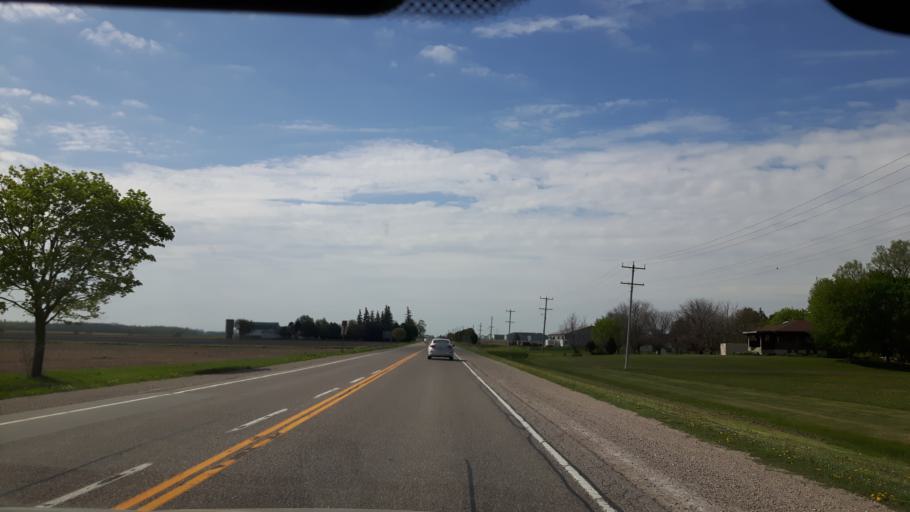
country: CA
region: Ontario
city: South Huron
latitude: 43.2872
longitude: -81.4686
